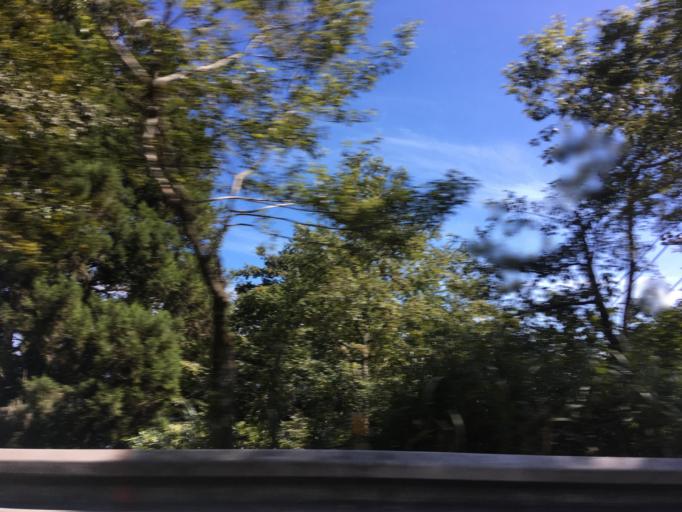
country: TW
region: Taiwan
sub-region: Yilan
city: Yilan
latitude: 24.5288
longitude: 121.5188
